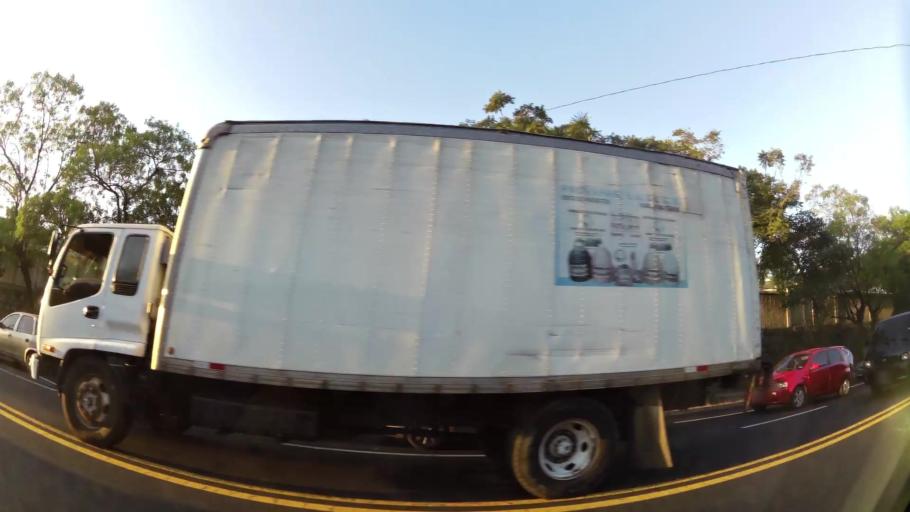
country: SV
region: San Salvador
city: San Salvador
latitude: 13.7035
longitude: -89.2094
